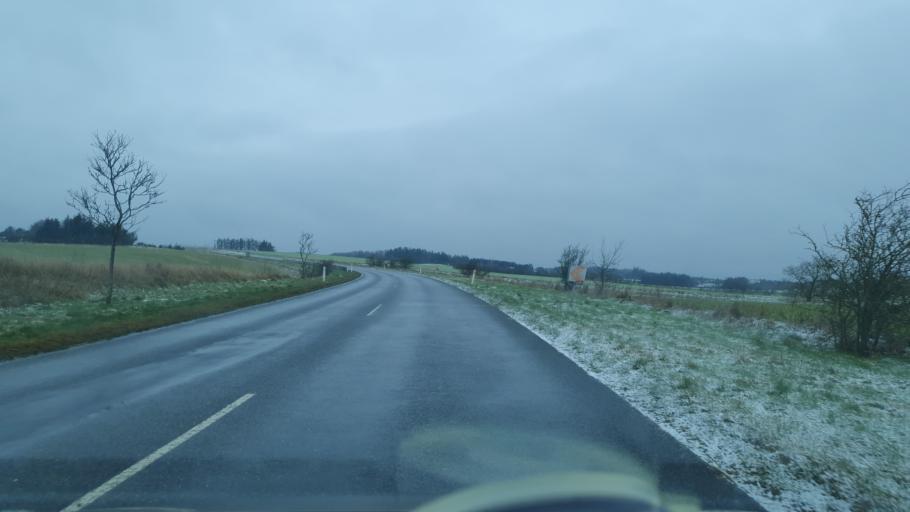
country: DK
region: North Denmark
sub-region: Jammerbugt Kommune
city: Brovst
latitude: 57.1244
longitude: 9.4892
